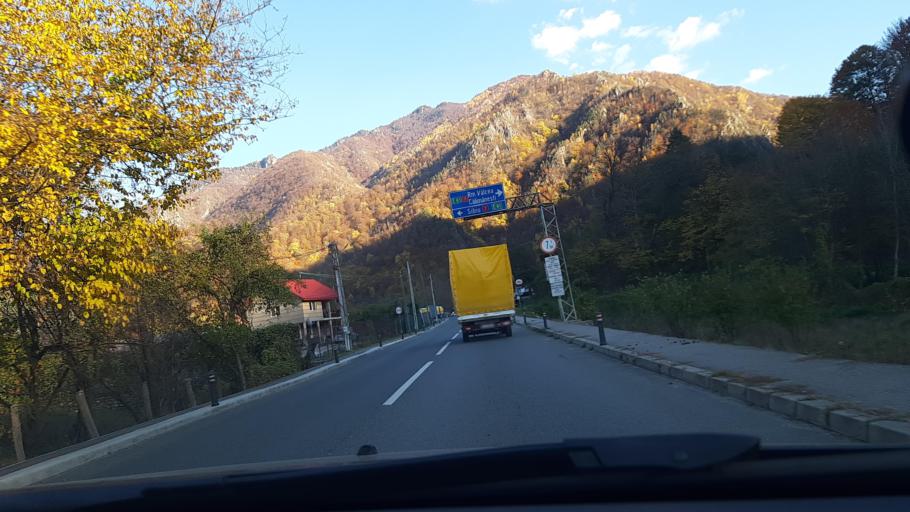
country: RO
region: Valcea
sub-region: Comuna Brezoi
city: Brezoi
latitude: 45.3330
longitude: 24.2730
